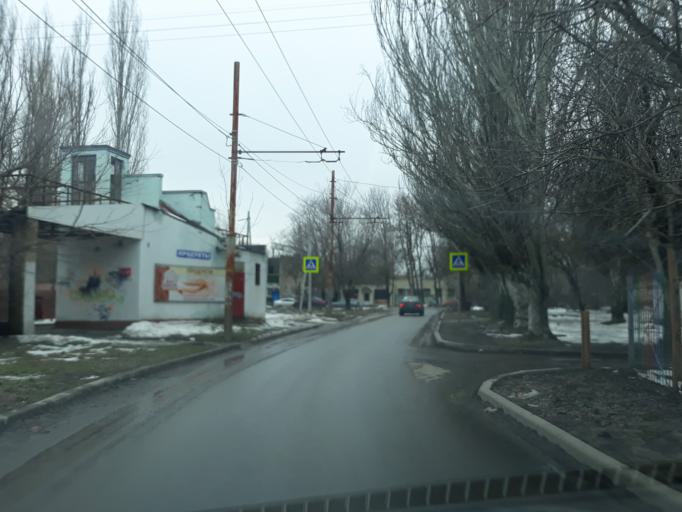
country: RU
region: Rostov
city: Taganrog
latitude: 47.2629
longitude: 38.9223
